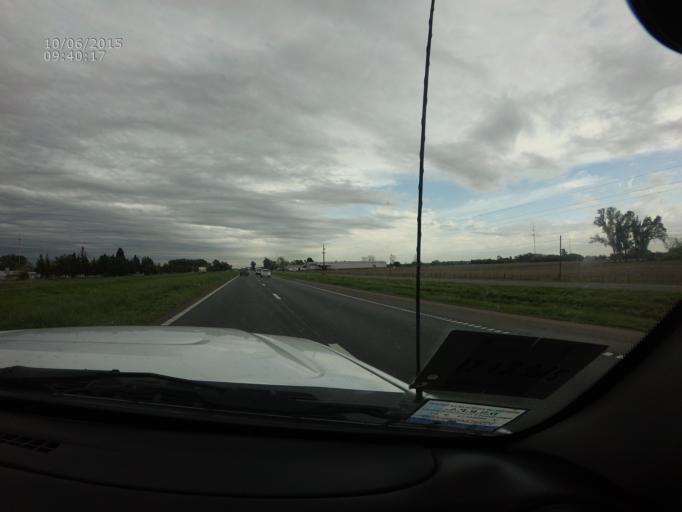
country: AR
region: Buenos Aires
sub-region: Partido de Zarate
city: Zarate
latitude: -34.0856
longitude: -59.1947
